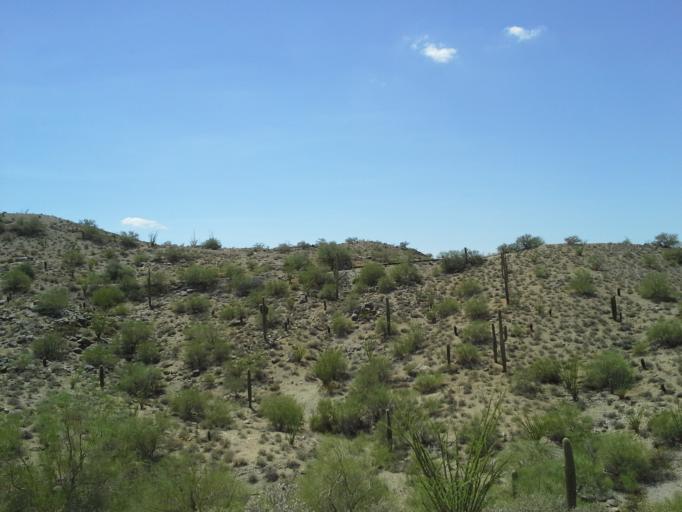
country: US
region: Arizona
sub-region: Maricopa County
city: Guadalupe
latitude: 33.3437
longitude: -112.0445
